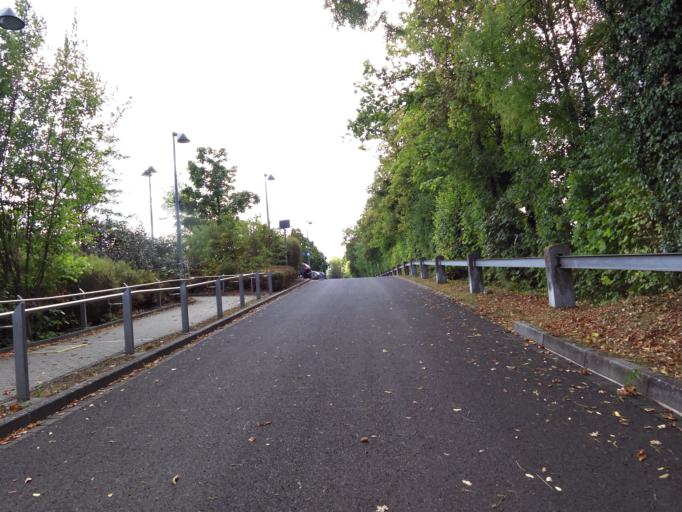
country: DE
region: Bavaria
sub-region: Regierungsbezirk Unterfranken
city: Veitshochheim
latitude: 49.8309
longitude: 9.8759
